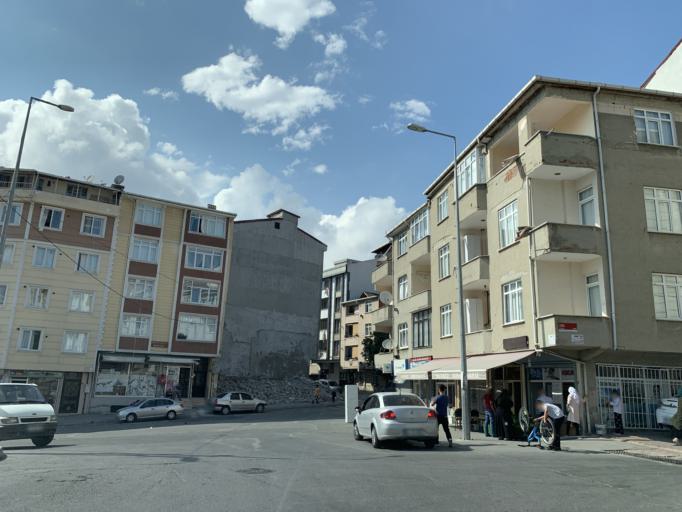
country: TR
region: Istanbul
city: Esenyurt
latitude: 41.0335
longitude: 28.6728
